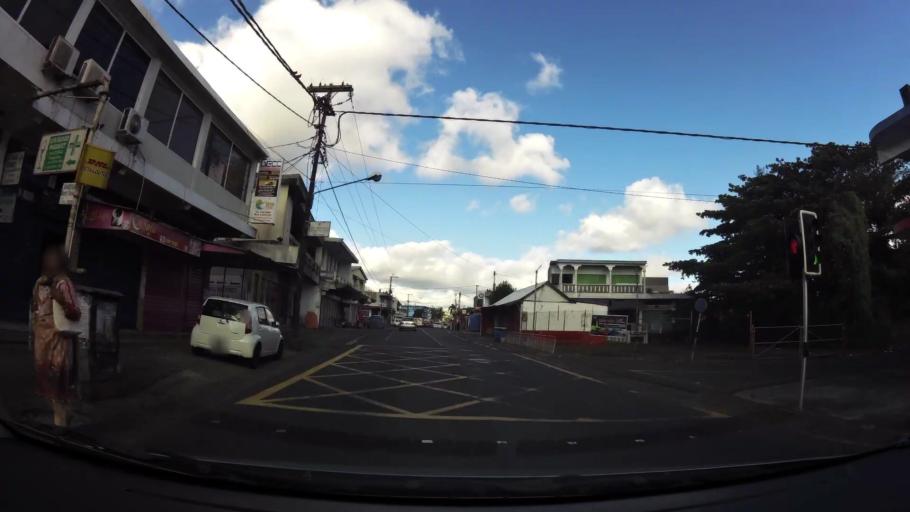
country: MU
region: Plaines Wilhems
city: Vacoas
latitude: -20.2830
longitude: 57.5042
